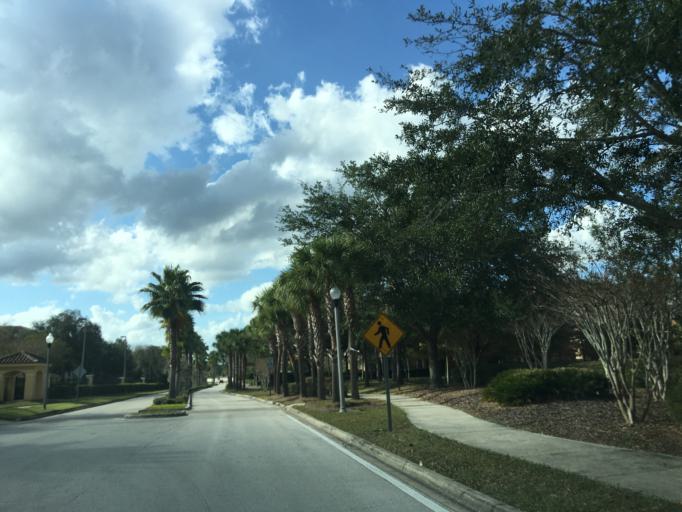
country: US
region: Florida
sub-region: Orange County
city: Eatonville
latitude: 28.6275
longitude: -81.4017
